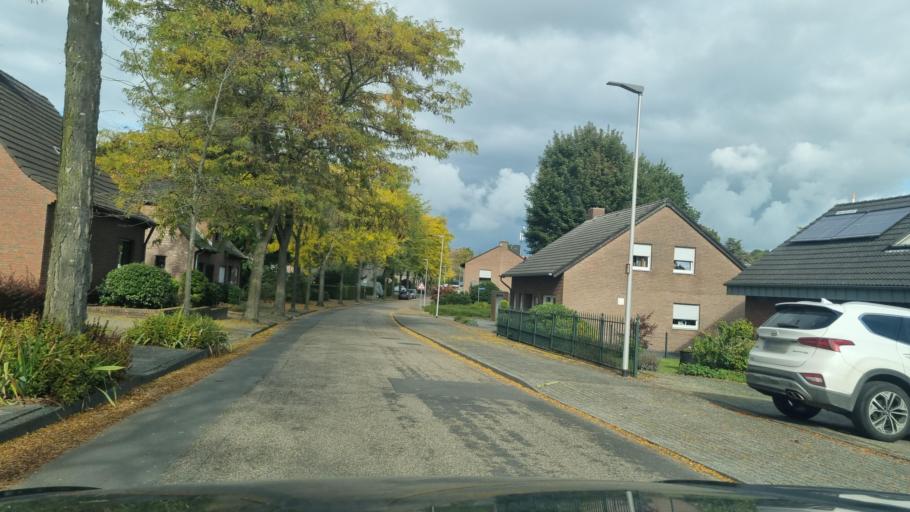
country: DE
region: North Rhine-Westphalia
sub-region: Regierungsbezirk Dusseldorf
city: Kleve
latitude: 51.7787
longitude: 6.1038
